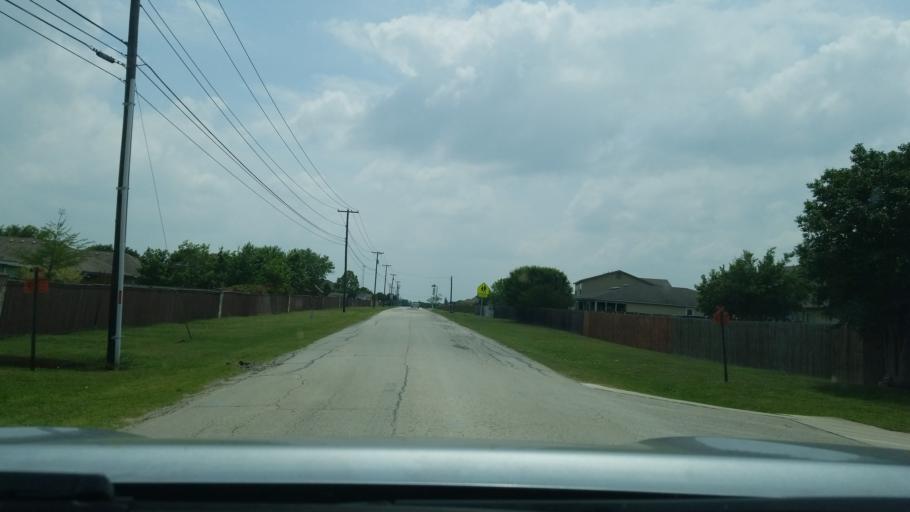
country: US
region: Texas
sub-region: Comal County
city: New Braunfels
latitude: 29.7543
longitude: -98.0680
